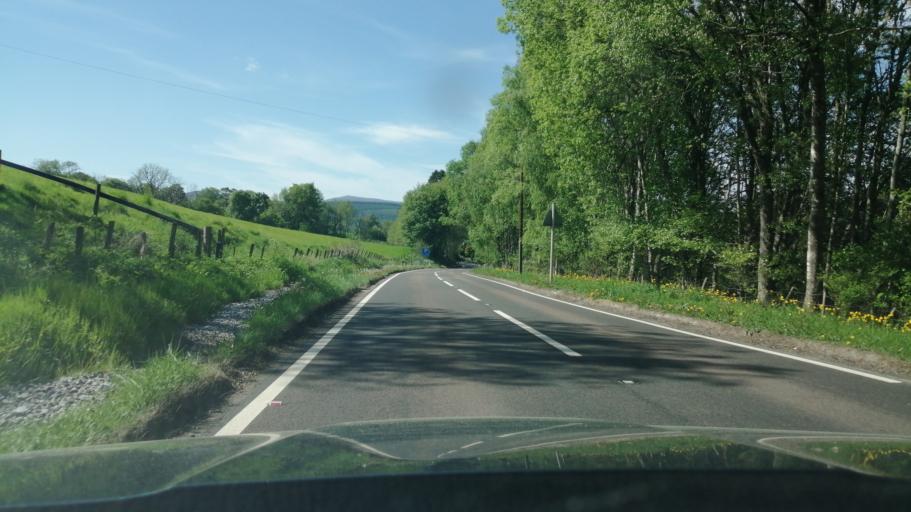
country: GB
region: Scotland
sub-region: Moray
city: Dufftown
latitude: 57.5006
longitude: -3.1364
